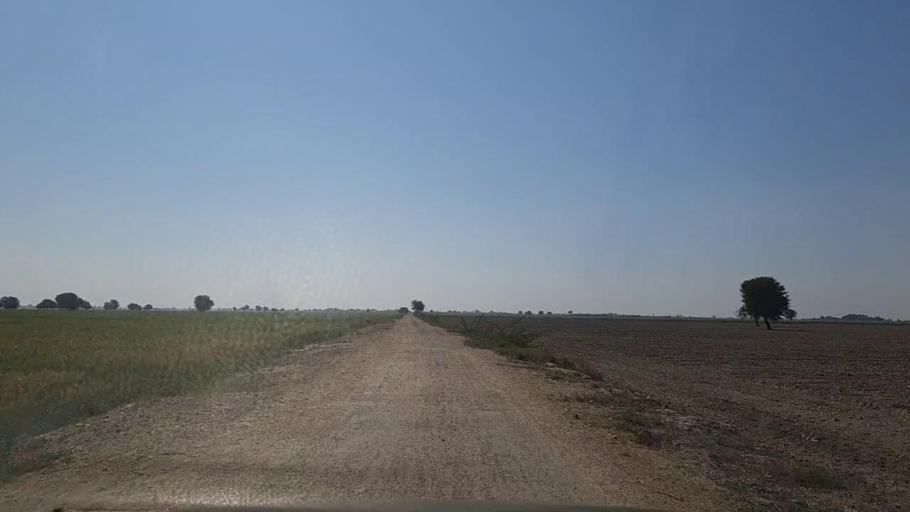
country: PK
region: Sindh
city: Pithoro
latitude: 25.4223
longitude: 69.3799
